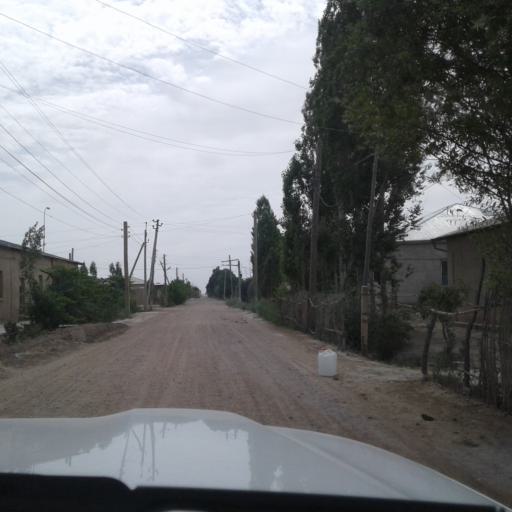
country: TM
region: Dasoguz
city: Tagta
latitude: 41.6003
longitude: 59.8500
